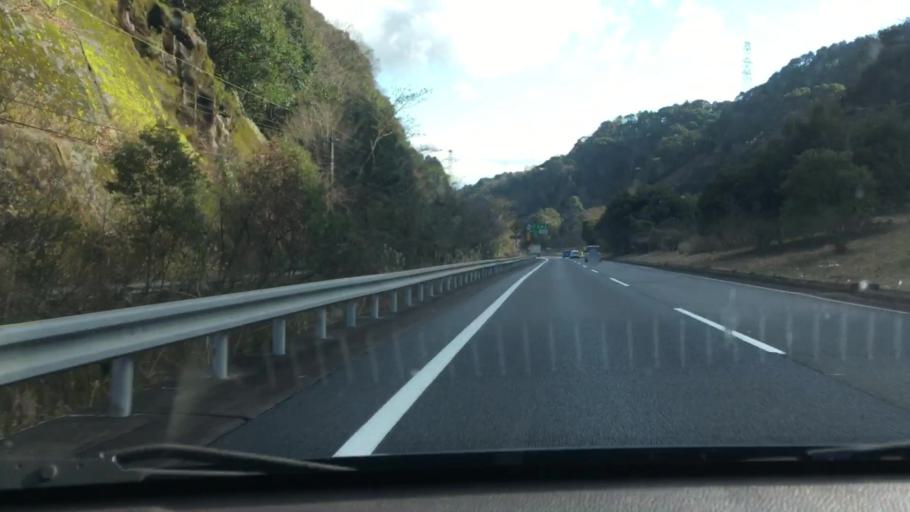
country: JP
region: Kumamoto
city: Hitoyoshi
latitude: 32.2710
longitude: 130.7598
